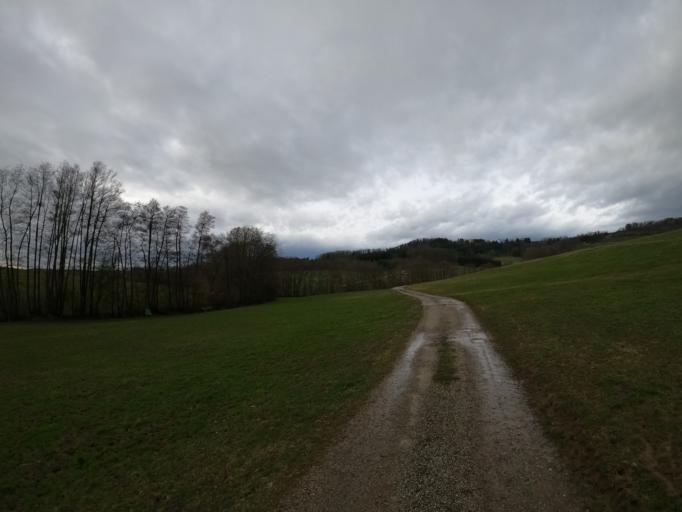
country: DE
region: Baden-Wuerttemberg
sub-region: Regierungsbezirk Stuttgart
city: Waschenbeuren
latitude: 48.7310
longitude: 9.6927
